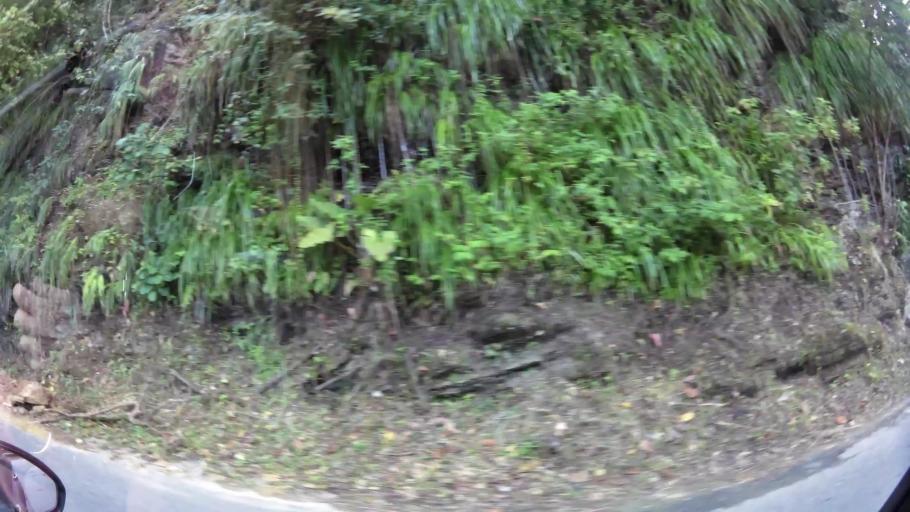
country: TT
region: Diego Martin
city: Petit Valley
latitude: 10.7518
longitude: -61.4779
